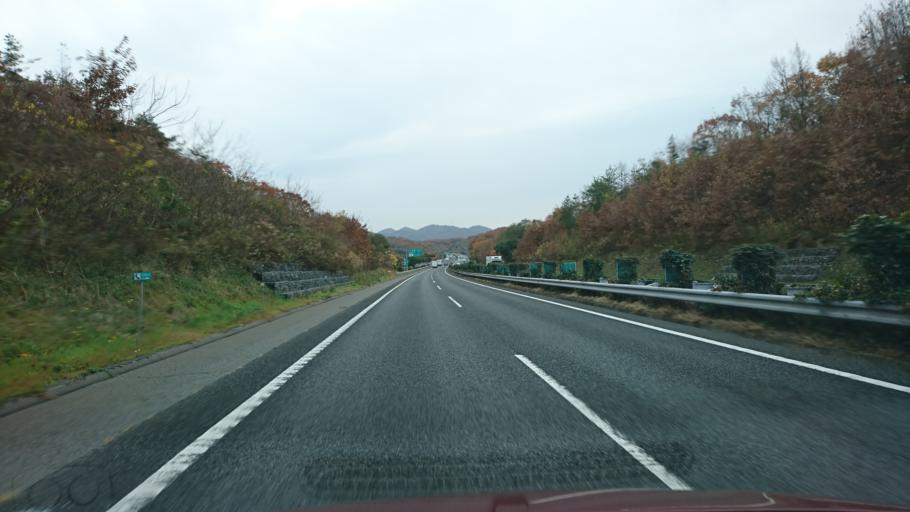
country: JP
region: Hyogo
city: Miki
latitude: 34.8015
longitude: 135.0431
